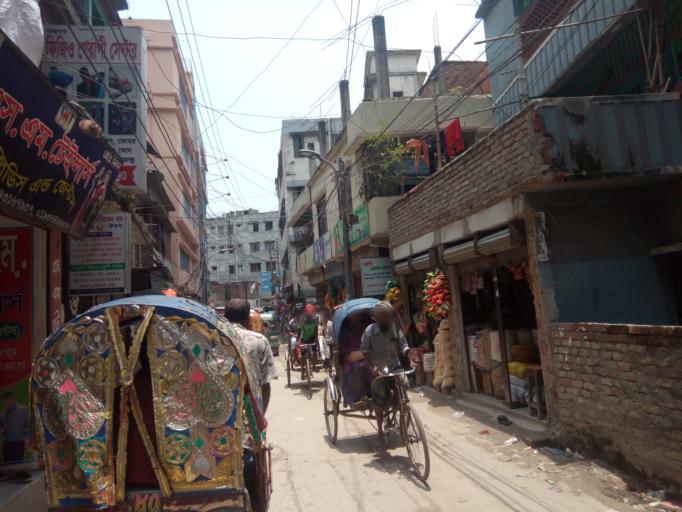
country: BD
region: Dhaka
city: Paltan
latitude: 23.7536
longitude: 90.4322
